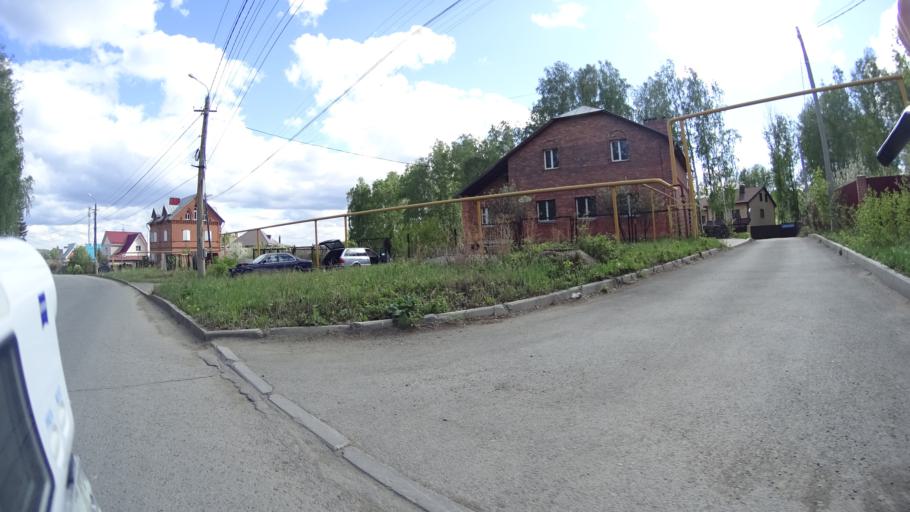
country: RU
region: Chelyabinsk
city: Sargazy
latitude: 55.1560
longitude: 61.2520
